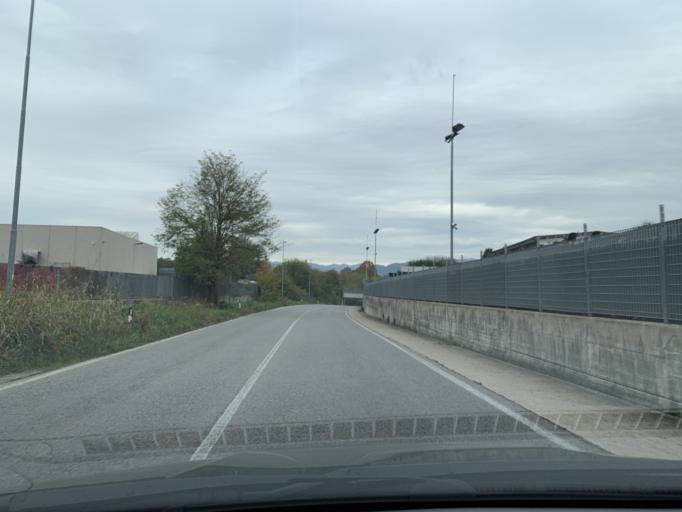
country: IT
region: Lombardy
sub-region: Provincia di Como
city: Vertemate Con Minoprio
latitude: 45.7348
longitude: 9.0663
